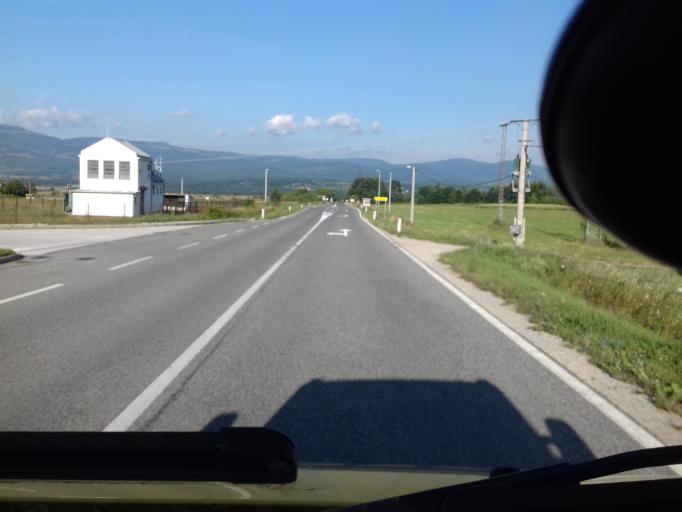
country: BA
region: Federation of Bosnia and Herzegovina
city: Orasac
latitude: 44.6357
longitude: 16.1814
